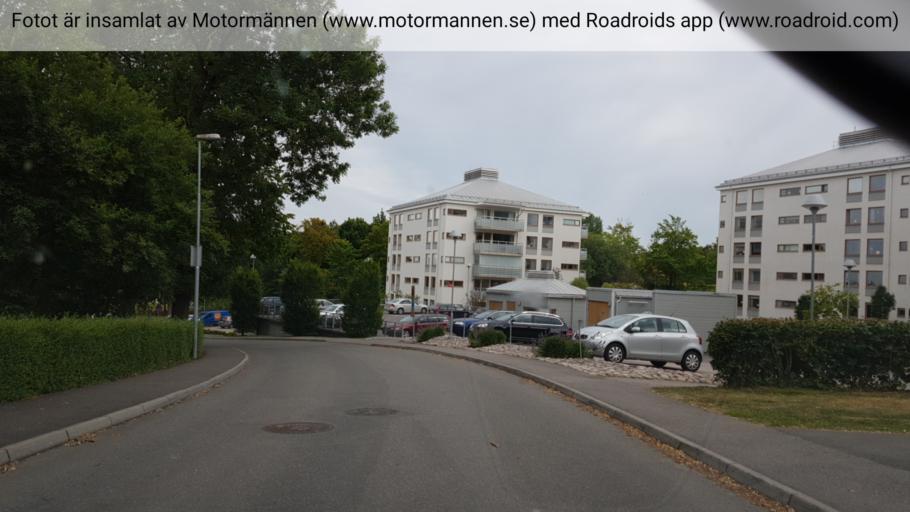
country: SE
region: Vaestra Goetaland
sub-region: Skovde Kommun
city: Skoevde
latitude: 58.3903
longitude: 13.8262
